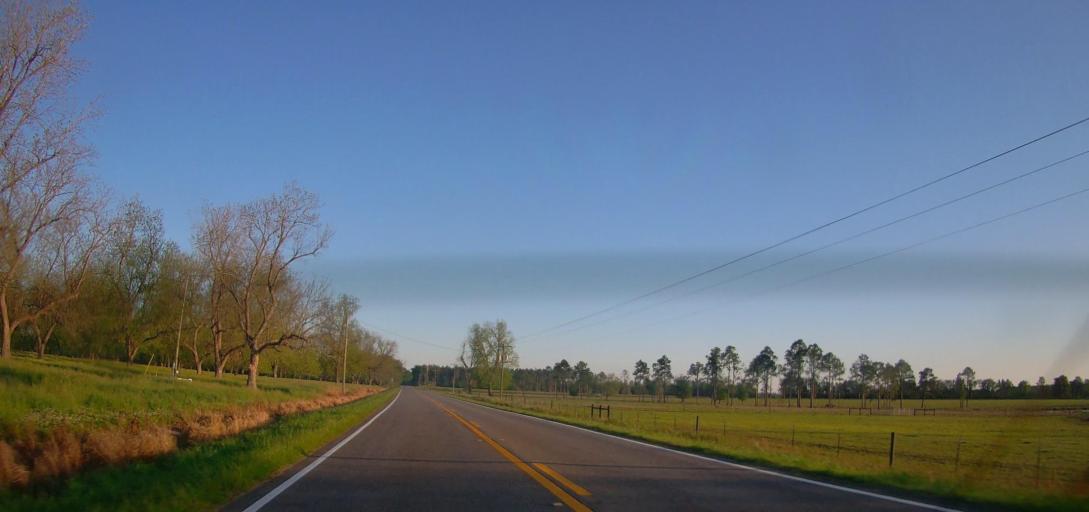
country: US
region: Georgia
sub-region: Irwin County
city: Ocilla
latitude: 31.6318
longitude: -83.2750
